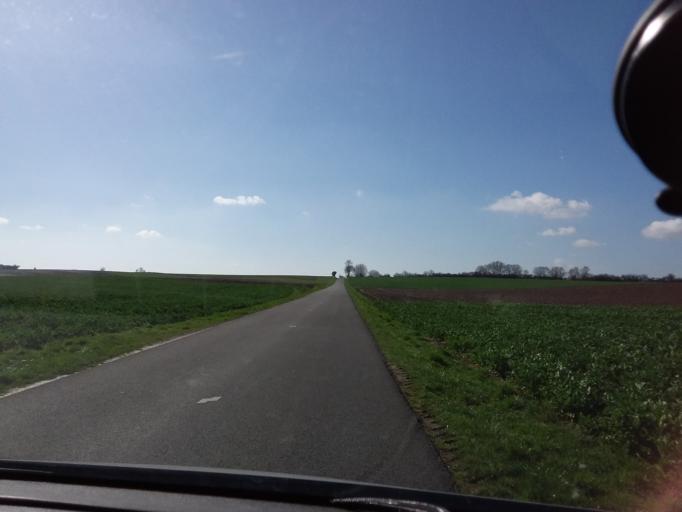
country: FR
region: Picardie
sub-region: Departement de l'Aisne
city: Hirson
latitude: 49.8972
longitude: 4.0984
